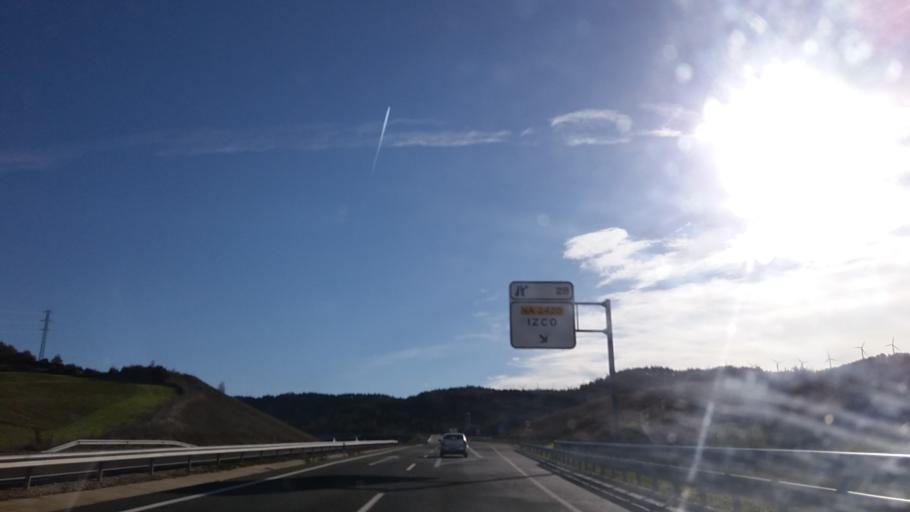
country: ES
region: Navarre
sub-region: Provincia de Navarra
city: Leache
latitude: 42.6595
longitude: -1.4200
